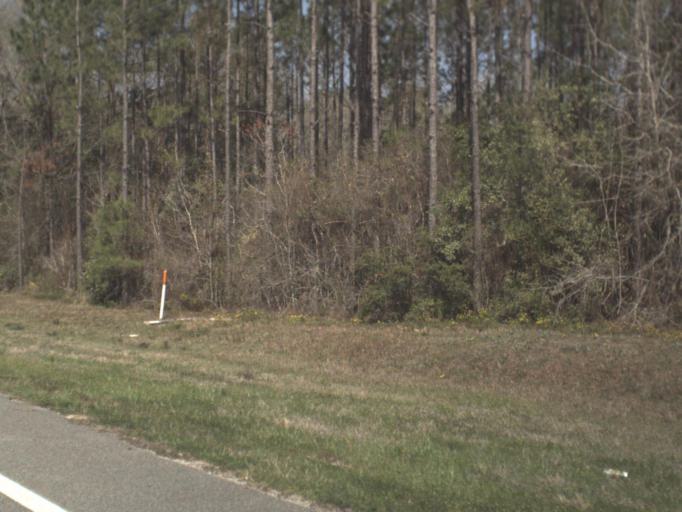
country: US
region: Florida
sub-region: Liberty County
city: Bristol
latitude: 30.3850
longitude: -84.7530
